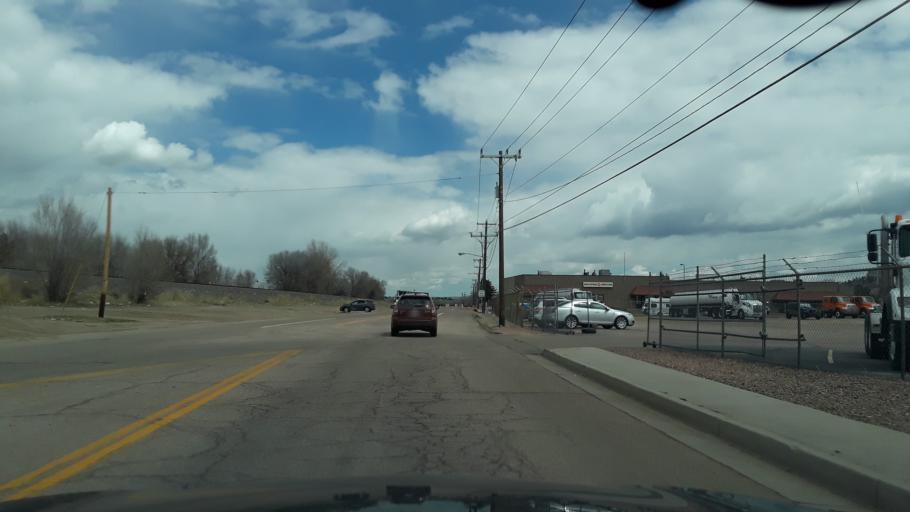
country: US
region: Colorado
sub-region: El Paso County
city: Colorado Springs
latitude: 38.8979
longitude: -104.8253
